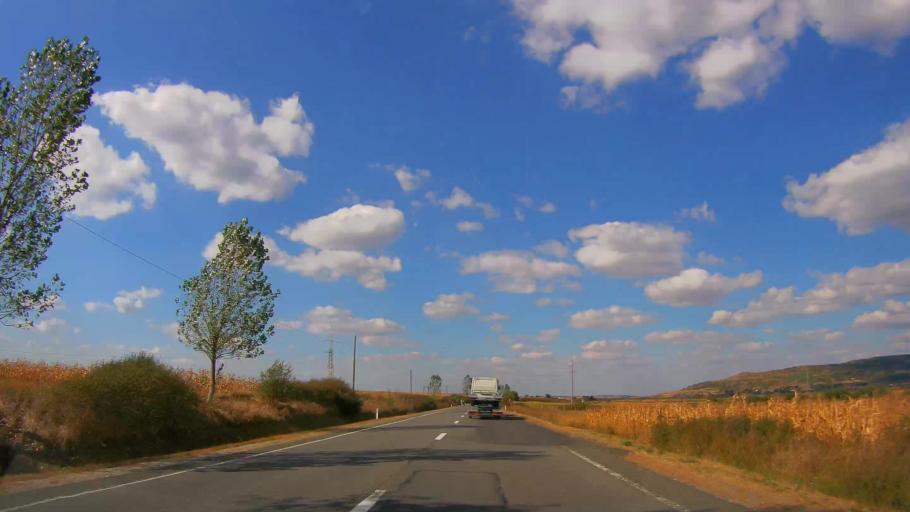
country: RO
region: Salaj
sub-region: Comuna Bobota
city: Dersida
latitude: 47.3680
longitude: 22.7902
